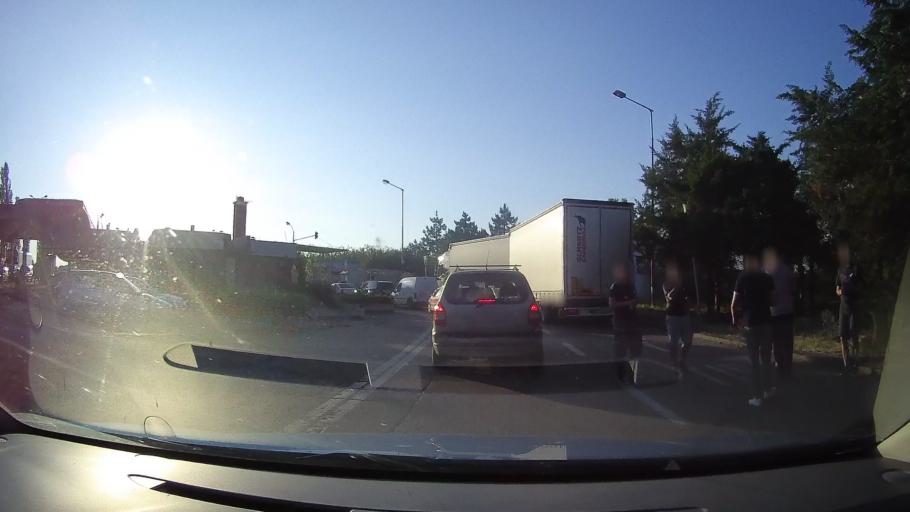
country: RO
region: Timis
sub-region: Comuna Moravita
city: Moravita
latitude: 45.2291
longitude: 21.2772
